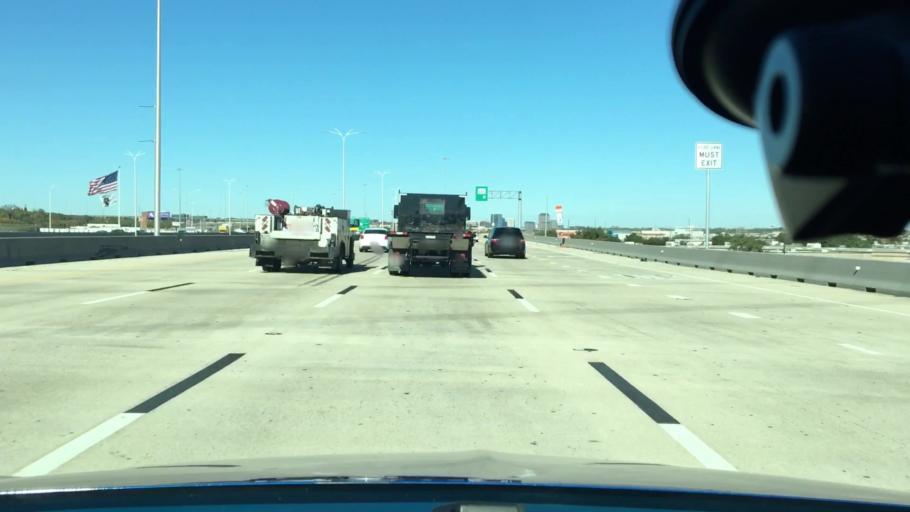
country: US
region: Texas
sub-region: Dallas County
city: Irving
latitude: 32.8312
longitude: -96.8909
